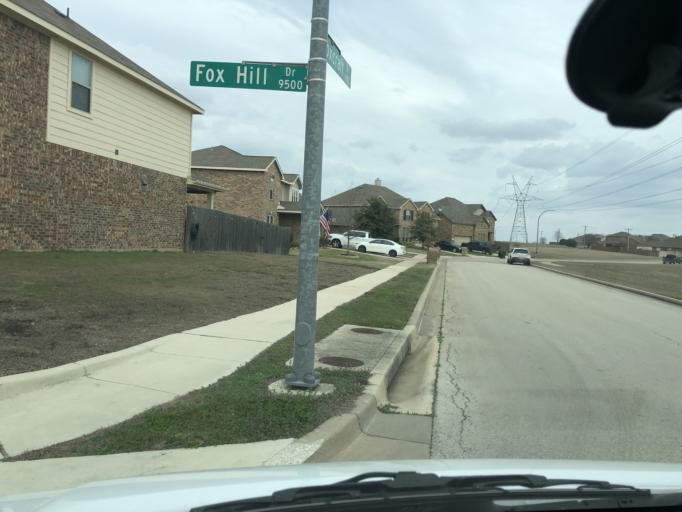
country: US
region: Texas
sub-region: Tarrant County
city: Saginaw
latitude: 32.9071
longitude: -97.3722
